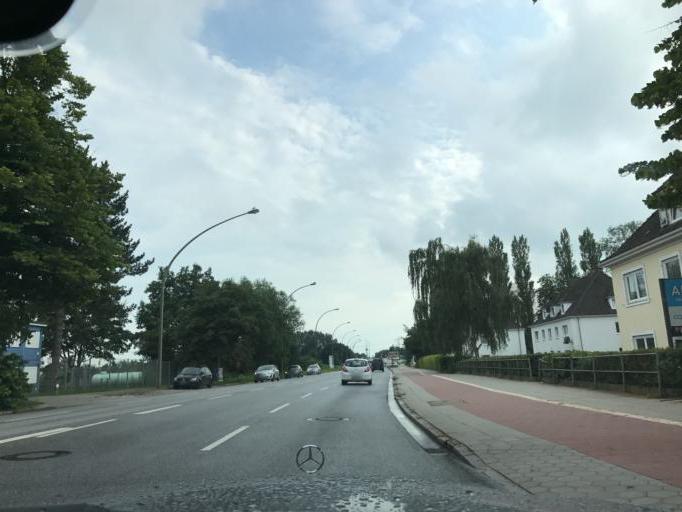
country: DE
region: Hamburg
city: Bergedorf
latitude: 53.4797
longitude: 10.2073
